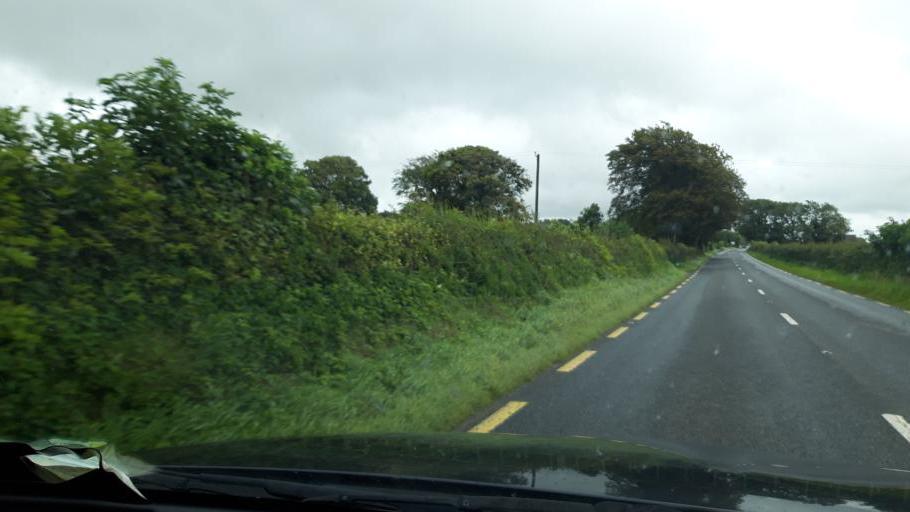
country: IE
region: Leinster
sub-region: Loch Garman
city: New Ross
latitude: 52.4327
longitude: -6.7903
